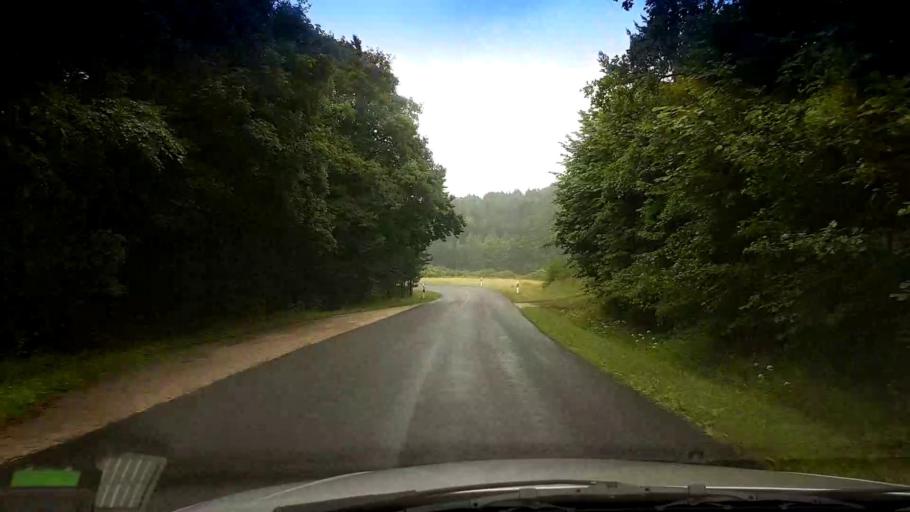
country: DE
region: Bavaria
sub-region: Upper Franconia
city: Altendorf
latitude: 50.0724
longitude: 11.1778
